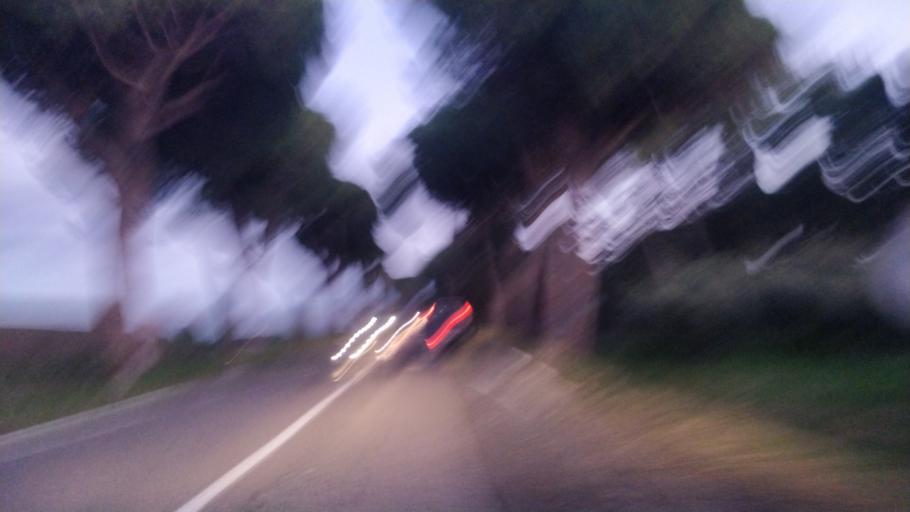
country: IT
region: Tuscany
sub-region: Provincia di Livorno
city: S.P. in Palazzi
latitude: 43.3347
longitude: 10.4917
